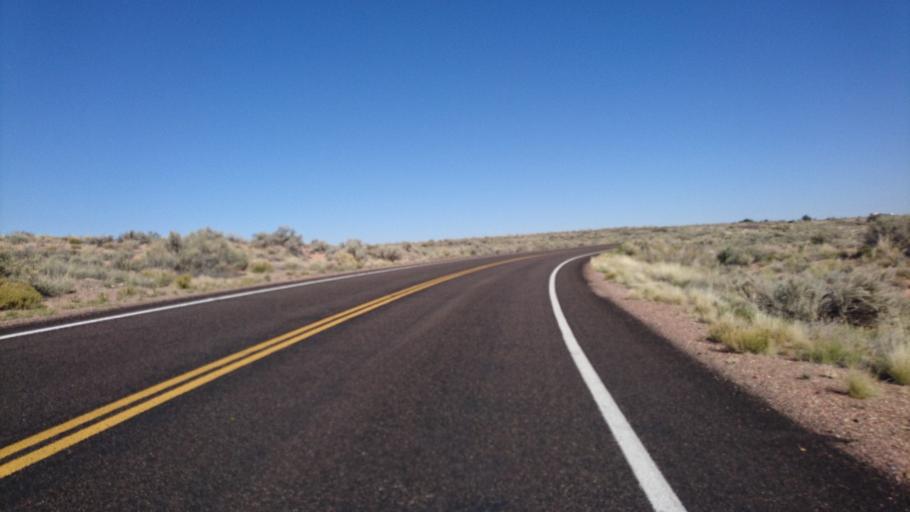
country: US
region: Arizona
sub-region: Navajo County
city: Holbrook
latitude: 35.0723
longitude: -109.7847
